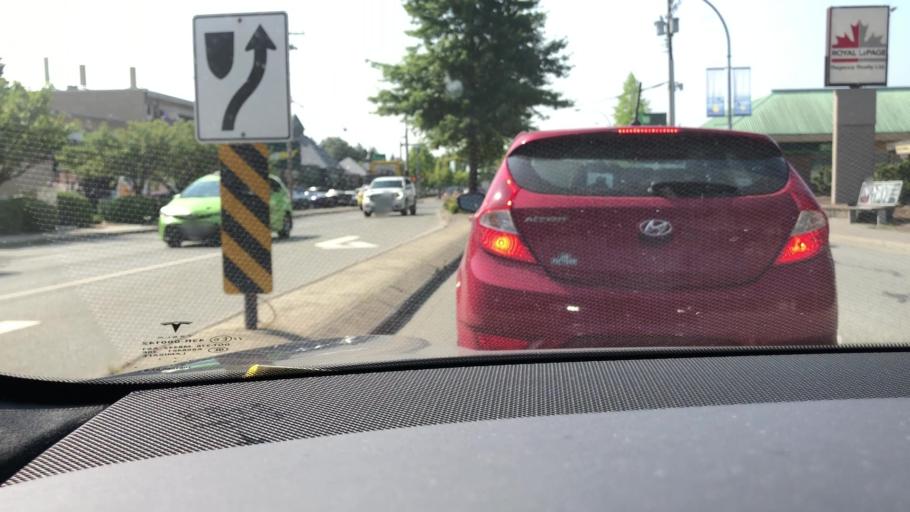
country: US
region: Washington
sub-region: Whatcom County
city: Point Roberts
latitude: 49.0274
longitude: -123.0688
